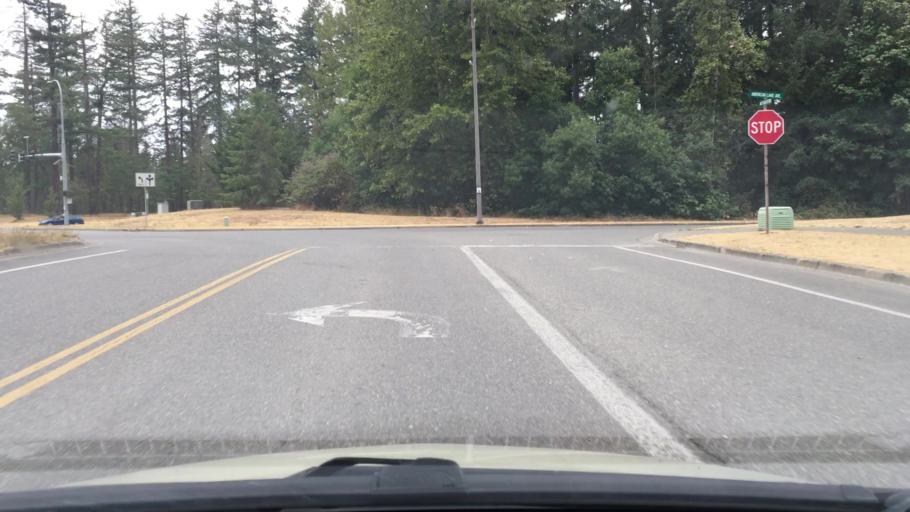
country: US
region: Washington
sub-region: Pierce County
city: Fort Lewis
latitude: 47.1105
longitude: -122.5921
